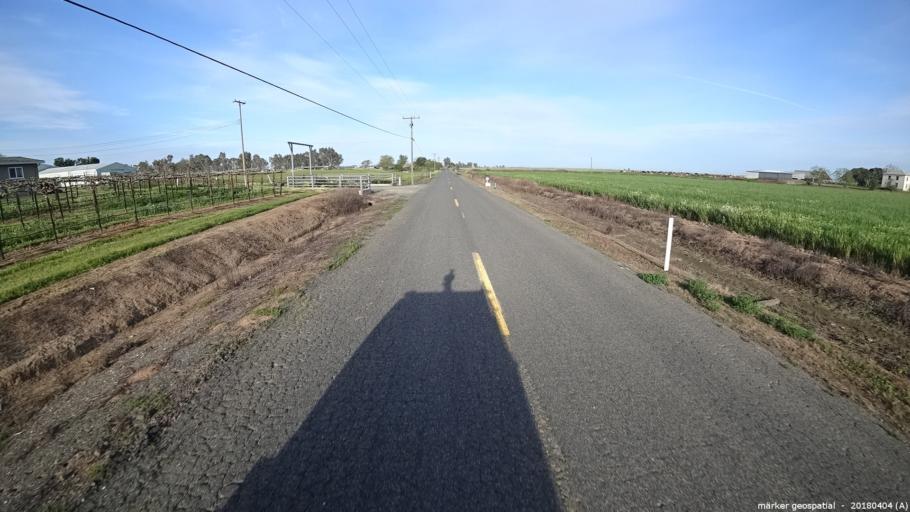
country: US
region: California
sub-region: Sacramento County
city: Herald
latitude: 38.3361
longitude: -121.2638
